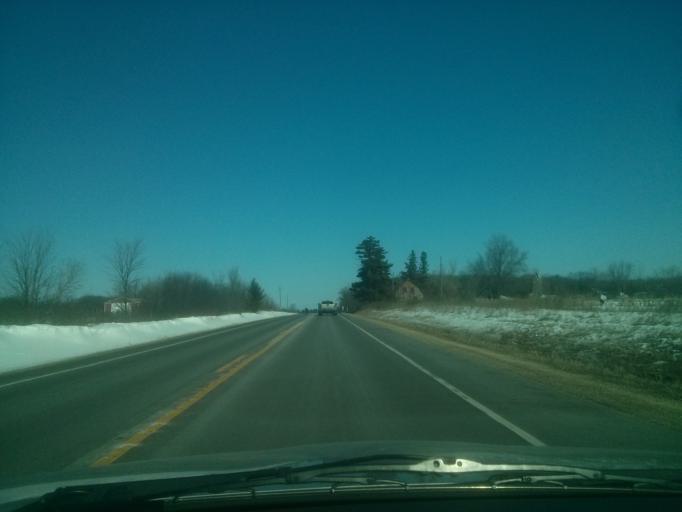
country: US
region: Wisconsin
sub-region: Polk County
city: Clear Lake
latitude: 45.1920
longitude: -92.2835
